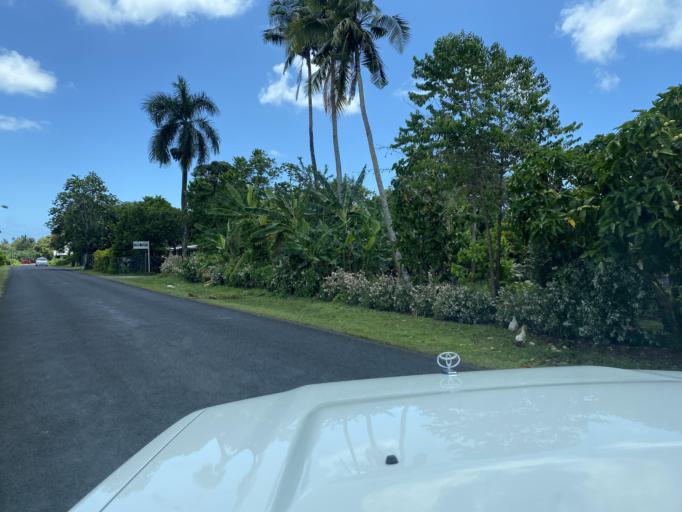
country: WS
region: Tuamasaga
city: Apia
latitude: -13.8395
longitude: -171.7570
